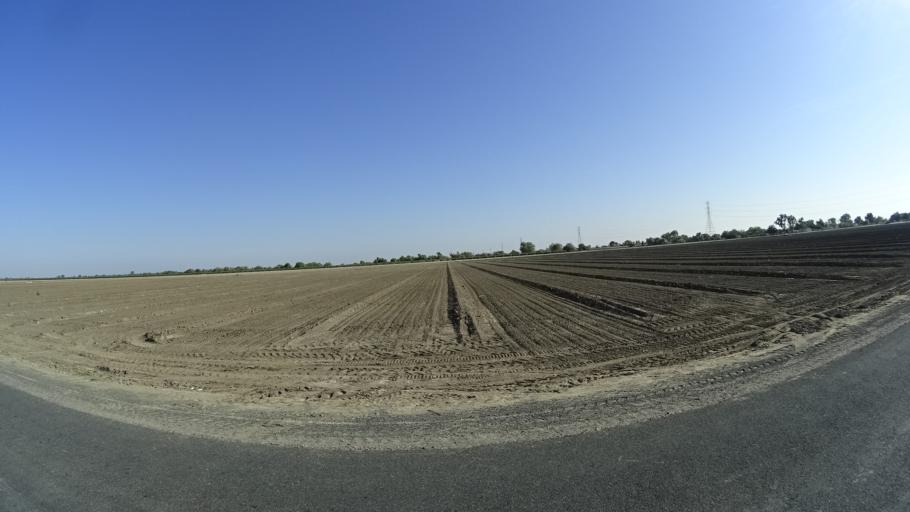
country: US
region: California
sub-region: Fresno County
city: Riverdale
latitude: 36.3766
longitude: -119.8931
